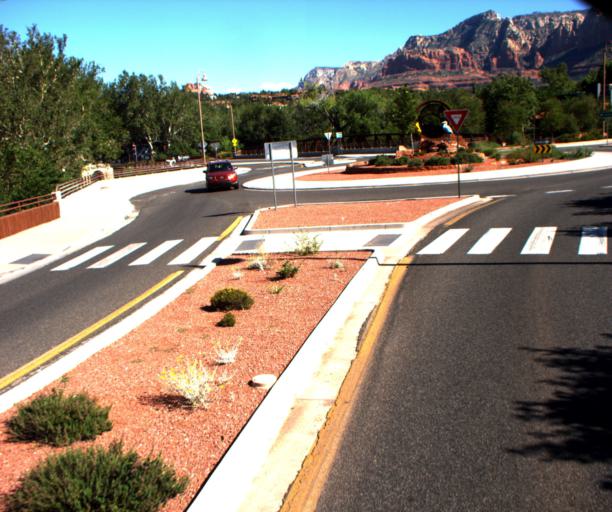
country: US
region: Arizona
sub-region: Coconino County
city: Sedona
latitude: 34.8616
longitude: -111.7616
